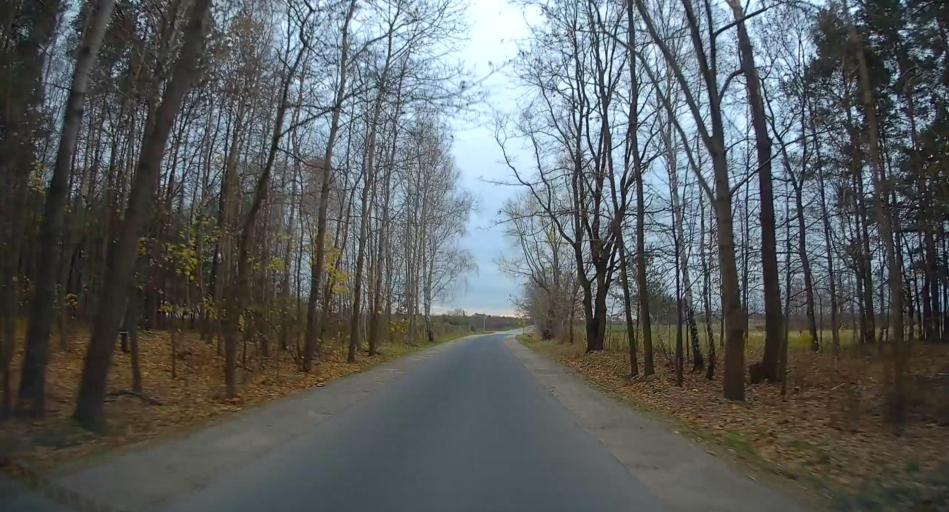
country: PL
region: Lodz Voivodeship
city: Zabia Wola
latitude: 52.0096
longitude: 20.6554
